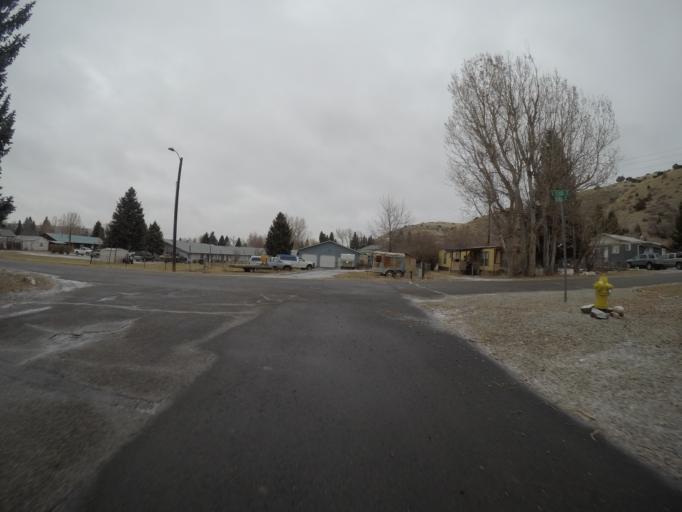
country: US
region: Montana
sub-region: Stillwater County
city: Absarokee
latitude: 45.5155
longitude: -109.4420
